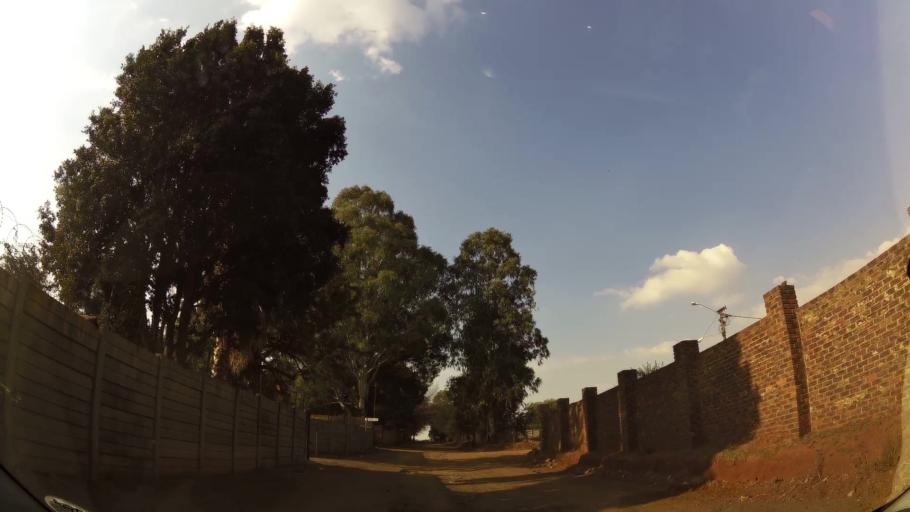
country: ZA
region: Gauteng
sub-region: Ekurhuleni Metropolitan Municipality
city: Benoni
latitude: -26.0979
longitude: 28.2880
